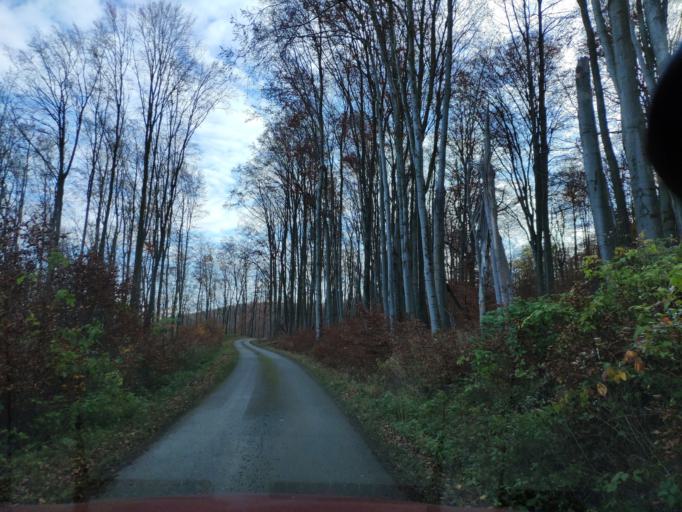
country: HU
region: Borsod-Abauj-Zemplen
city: Gonc
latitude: 48.5840
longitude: 21.4711
